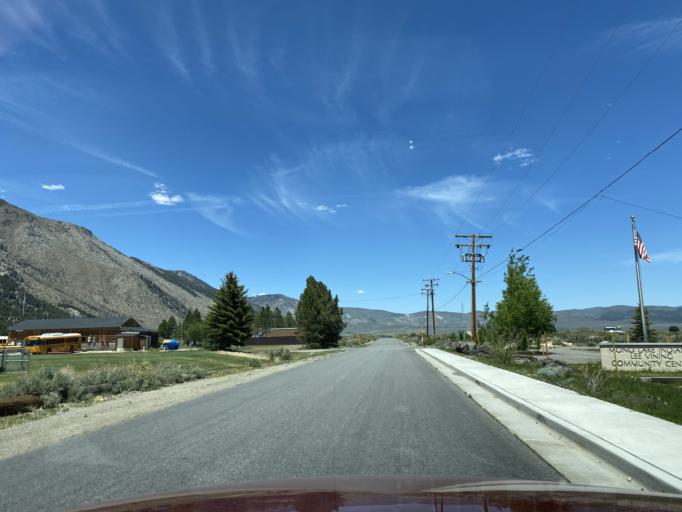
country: US
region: California
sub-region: Mono County
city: Bridgeport
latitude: 37.9610
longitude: -119.1198
